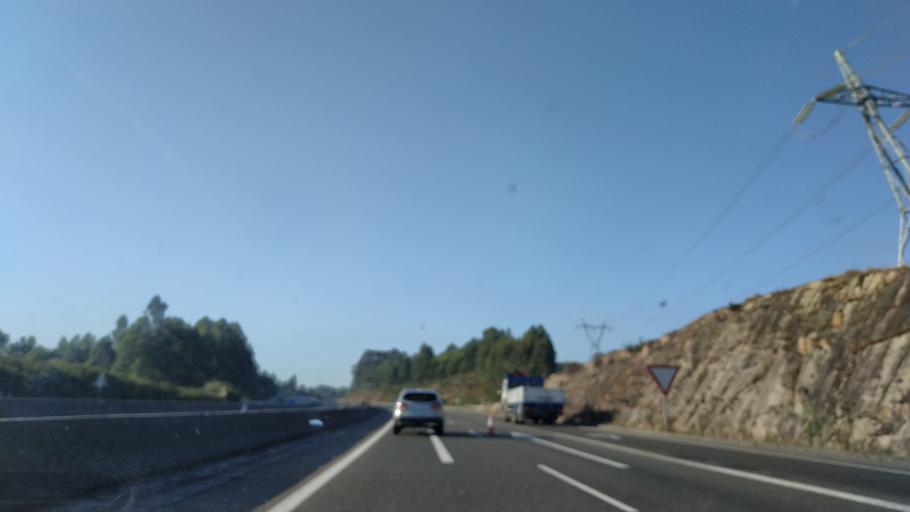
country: ES
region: Galicia
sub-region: Provincia da Coruna
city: Arteixo
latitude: 43.3053
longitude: -8.4751
